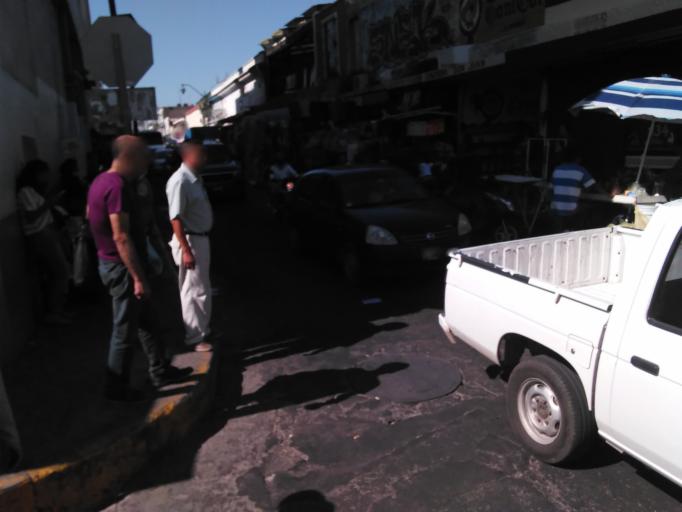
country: MX
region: Nayarit
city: Tepic
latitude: 21.5104
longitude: -104.8931
